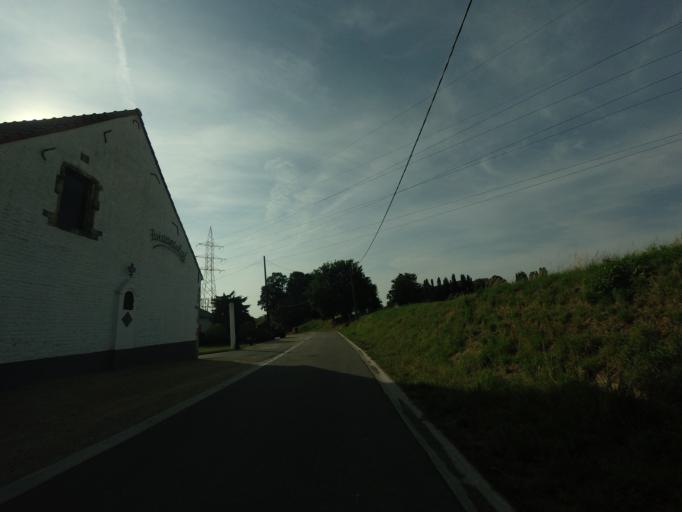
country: BE
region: Flanders
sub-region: Provincie Vlaams-Brabant
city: Meise
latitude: 50.9193
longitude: 4.3462
